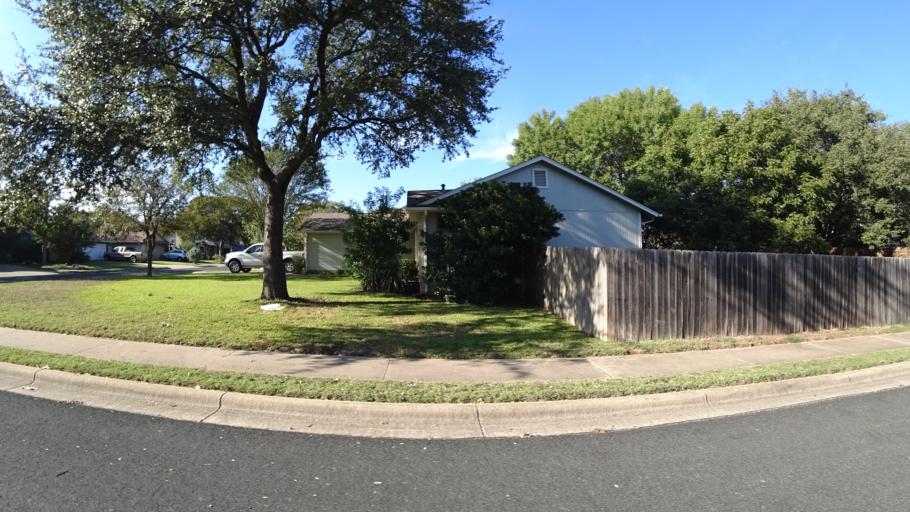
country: US
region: Texas
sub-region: Travis County
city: Shady Hollow
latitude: 30.2077
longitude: -97.8519
